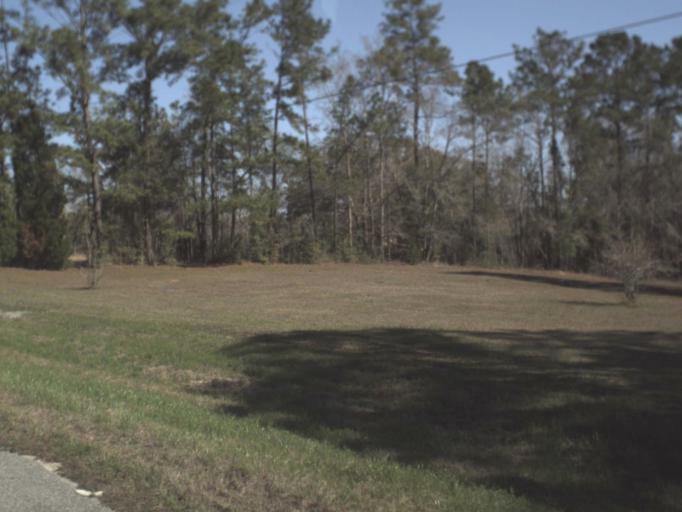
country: US
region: Florida
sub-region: Jefferson County
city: Monticello
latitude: 30.3930
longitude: -84.0136
